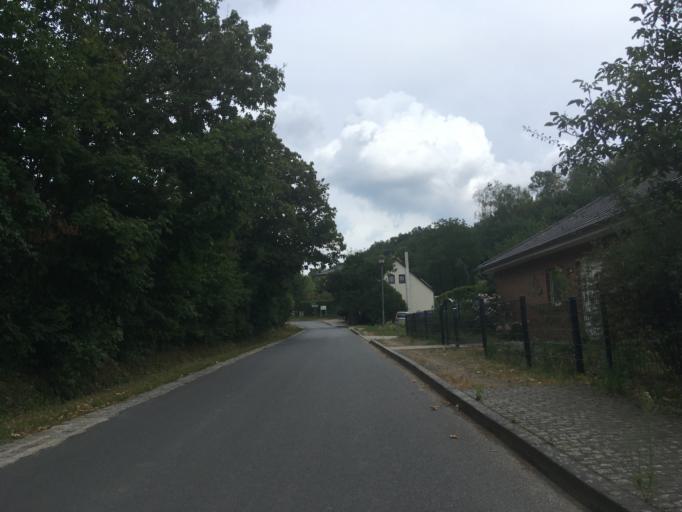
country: DE
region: Brandenburg
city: Chorin
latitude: 52.9000
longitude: 13.8681
